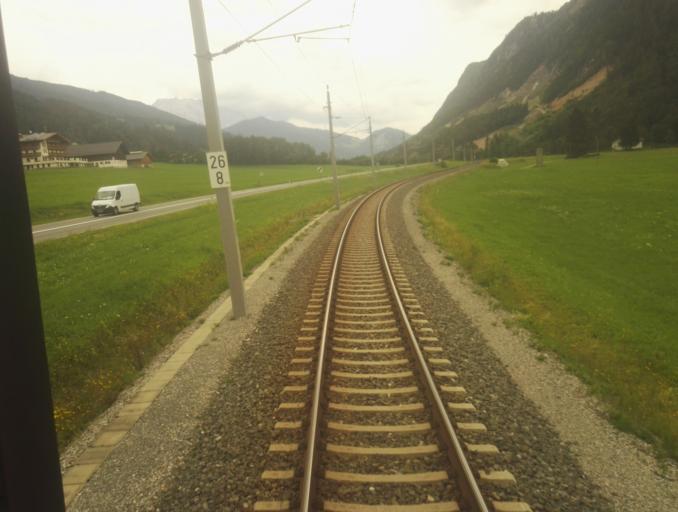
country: AT
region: Salzburg
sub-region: Politischer Bezirk Sankt Johann im Pongau
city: Forstau
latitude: 47.3907
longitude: 13.5012
